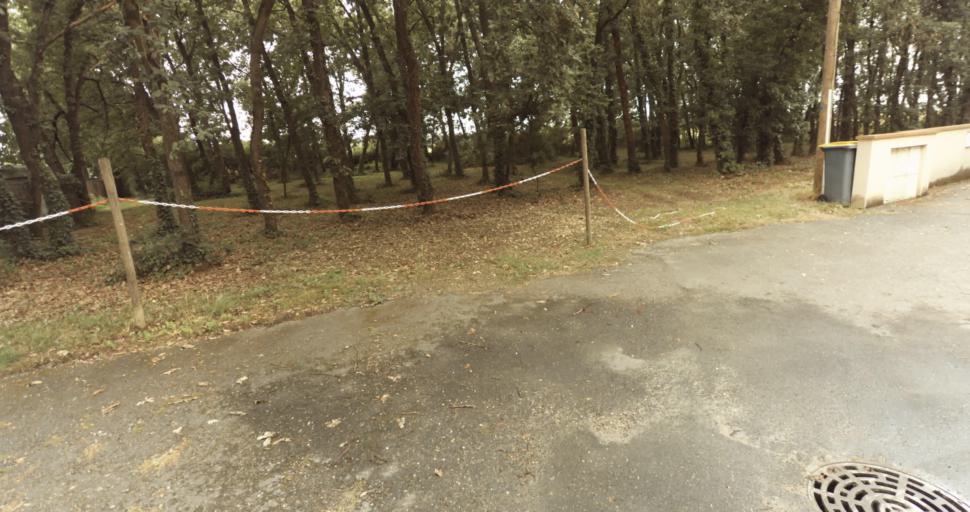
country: FR
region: Midi-Pyrenees
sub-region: Departement de la Haute-Garonne
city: Fonsorbes
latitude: 43.5524
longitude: 1.2258
